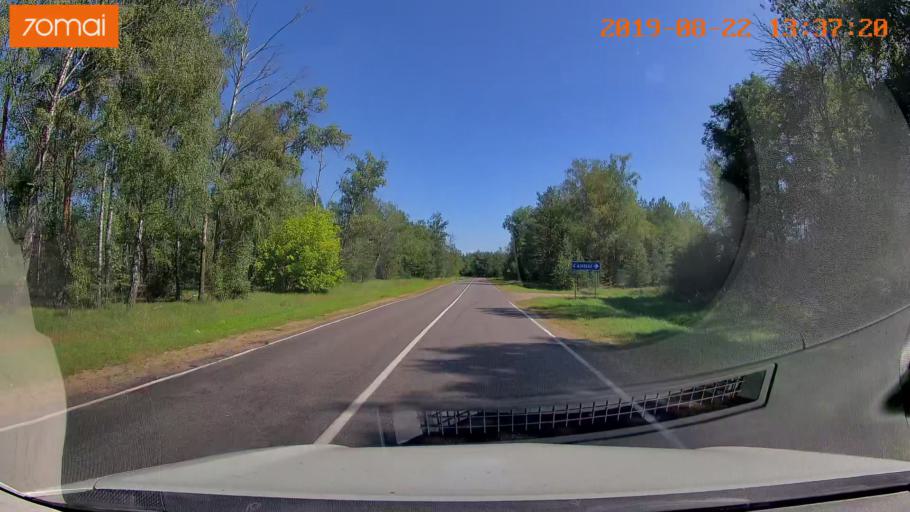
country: BY
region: Minsk
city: Staryya Darohi
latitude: 53.2171
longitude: 28.2969
